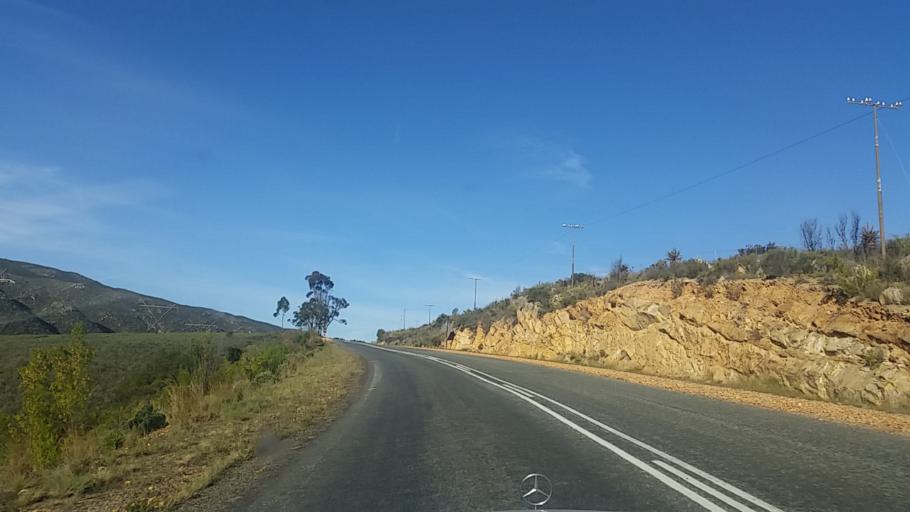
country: ZA
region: Western Cape
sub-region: Eden District Municipality
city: Knysna
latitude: -33.7528
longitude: 22.9489
